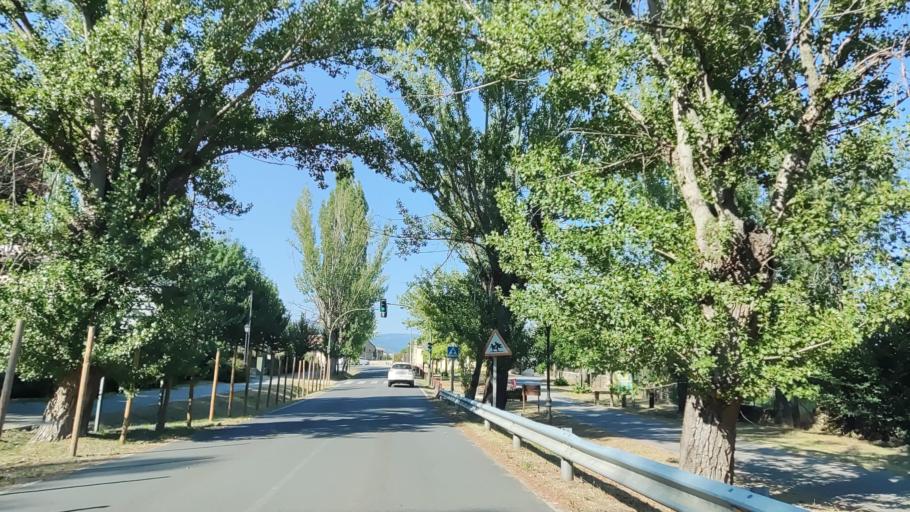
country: ES
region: Madrid
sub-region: Provincia de Madrid
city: Rascafria
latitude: 40.9007
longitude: -3.8790
